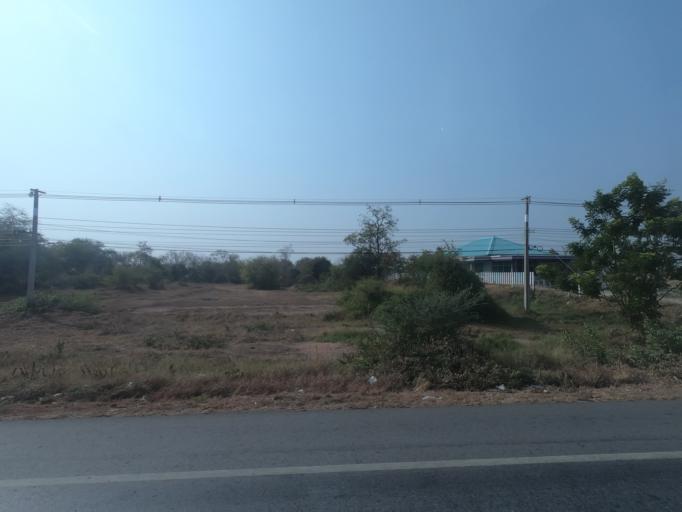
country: TH
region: Khon Kaen
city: Non Sila
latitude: 15.9804
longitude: 102.6956
